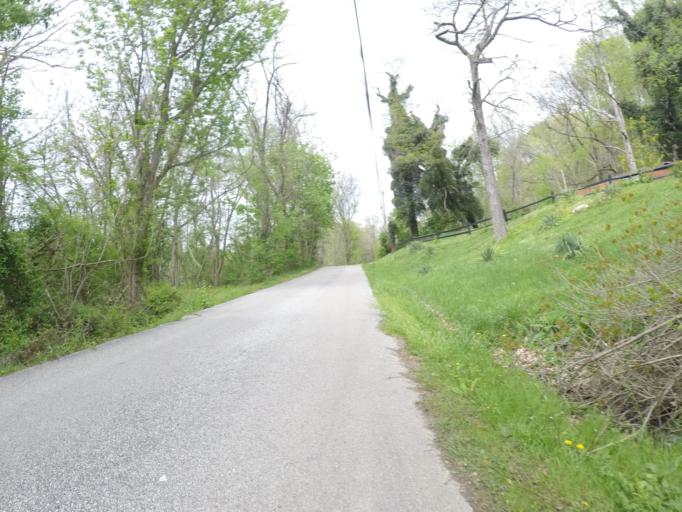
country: US
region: West Virginia
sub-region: Cabell County
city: Huntington
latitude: 38.3963
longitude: -82.4858
